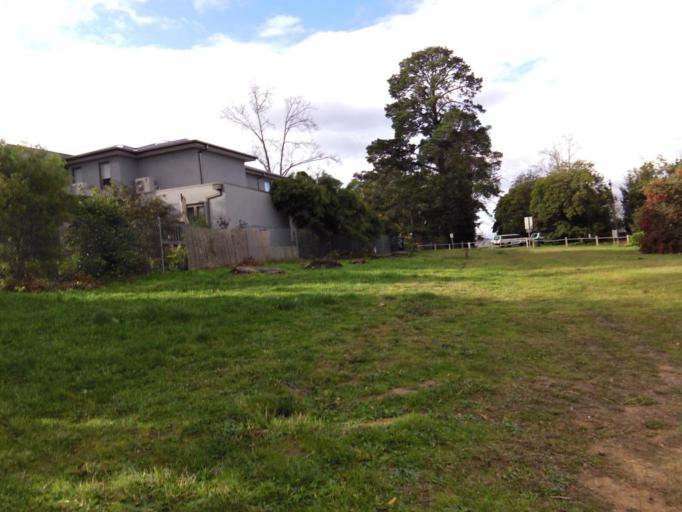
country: AU
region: Victoria
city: Mitcham
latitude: -37.8184
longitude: 145.2108
